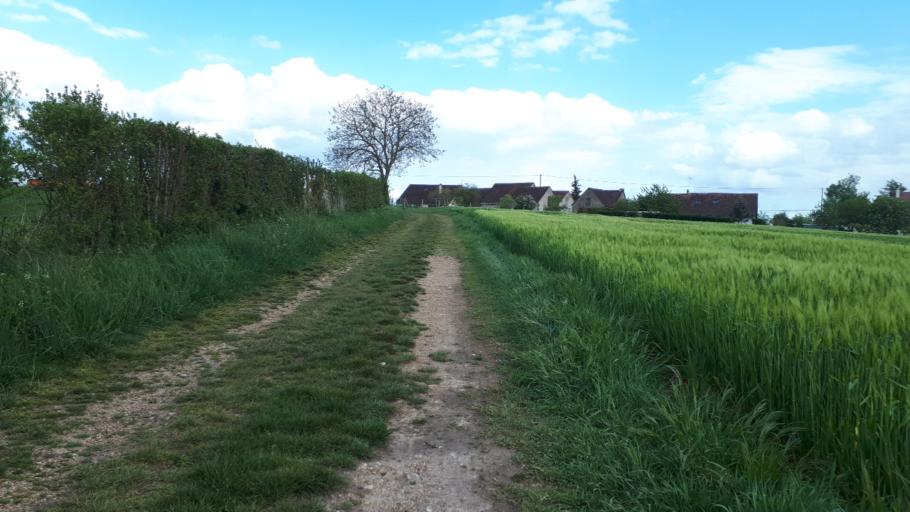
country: FR
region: Centre
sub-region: Departement du Loir-et-Cher
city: Aze
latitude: 47.8364
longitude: 1.0007
